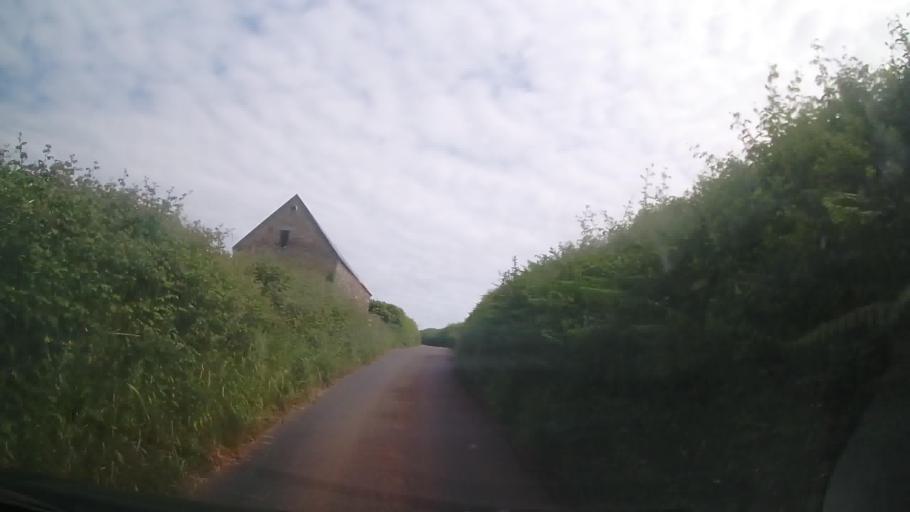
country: GB
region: England
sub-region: Devon
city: Salcombe
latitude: 50.2388
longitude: -3.6776
